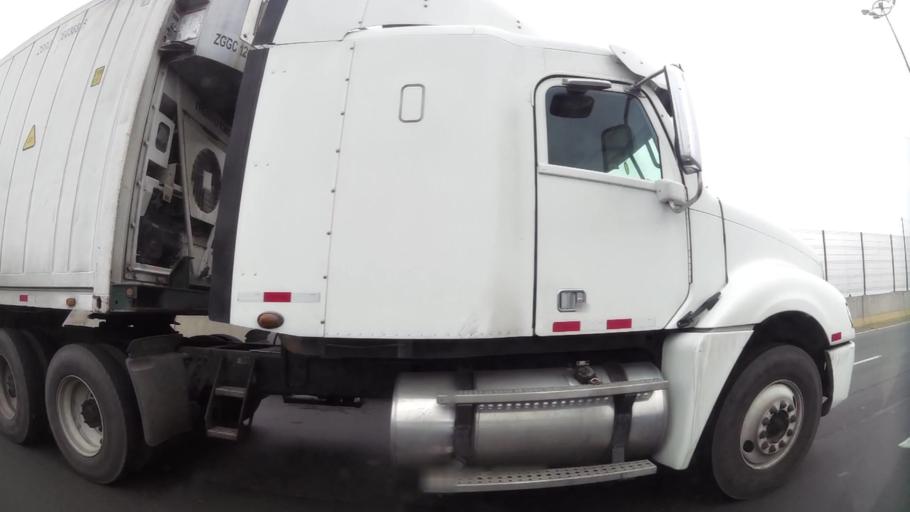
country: PE
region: Lima
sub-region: Lima
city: San Luis
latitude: -12.0392
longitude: -76.9882
